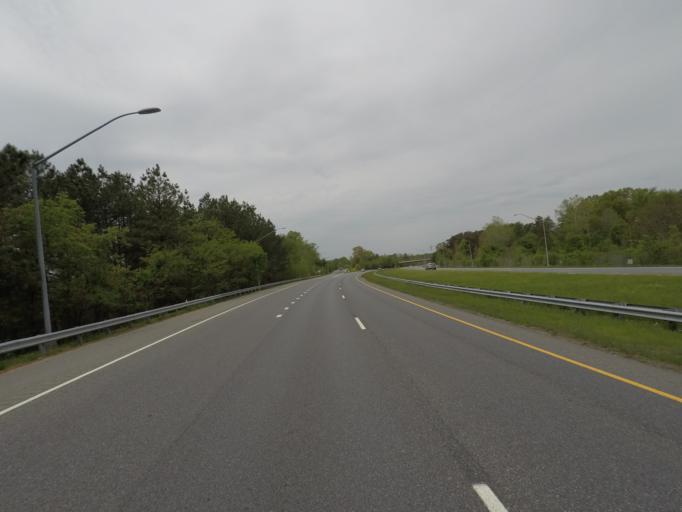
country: US
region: Maryland
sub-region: Anne Arundel County
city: Fort Meade
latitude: 39.0888
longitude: -76.7523
